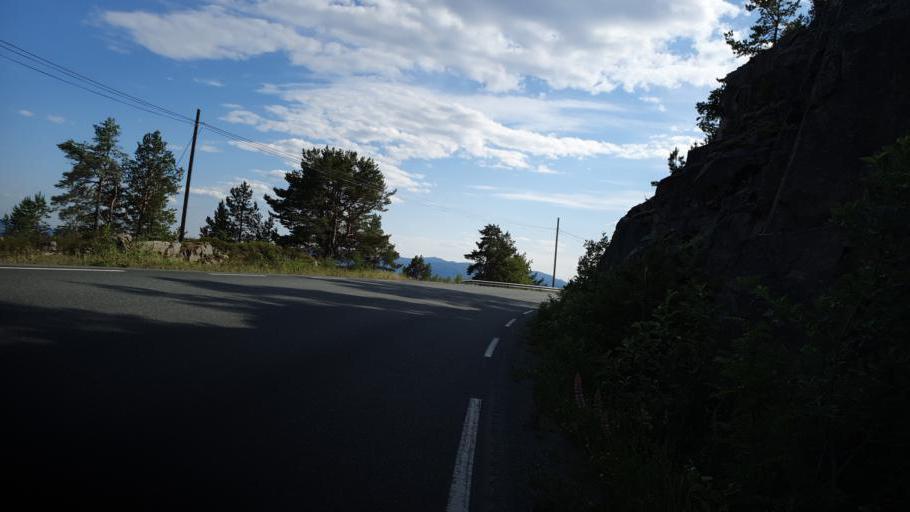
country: NO
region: Sor-Trondelag
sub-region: Trondheim
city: Trondheim
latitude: 63.5677
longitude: 10.3417
